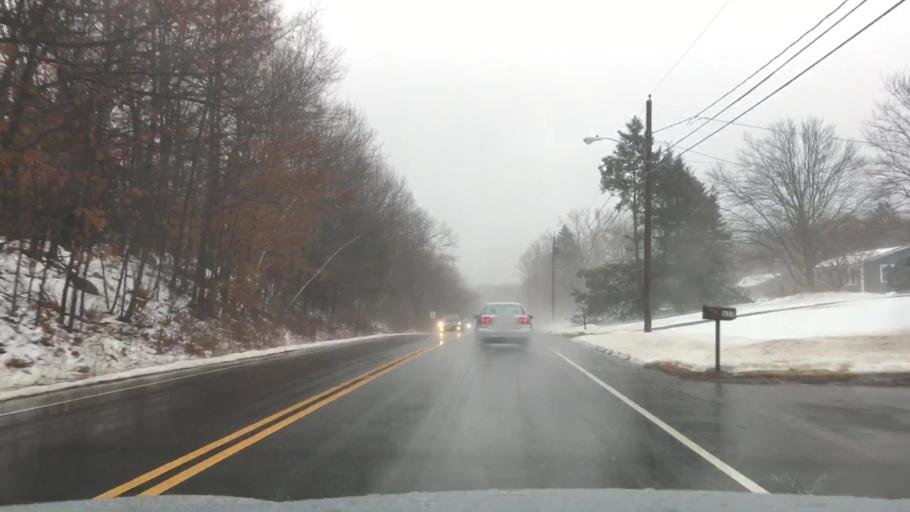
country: US
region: Massachusetts
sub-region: Hampden County
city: Ludlow
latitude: 42.2002
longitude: -72.4955
